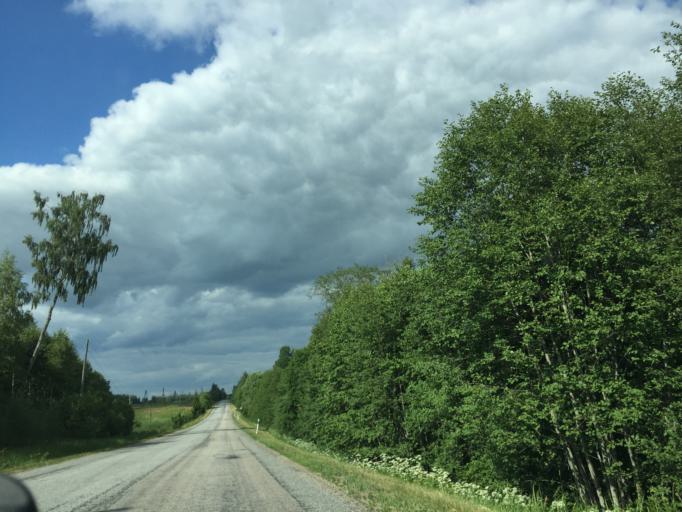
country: LV
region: Skriveri
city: Skriveri
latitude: 56.8140
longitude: 25.1160
